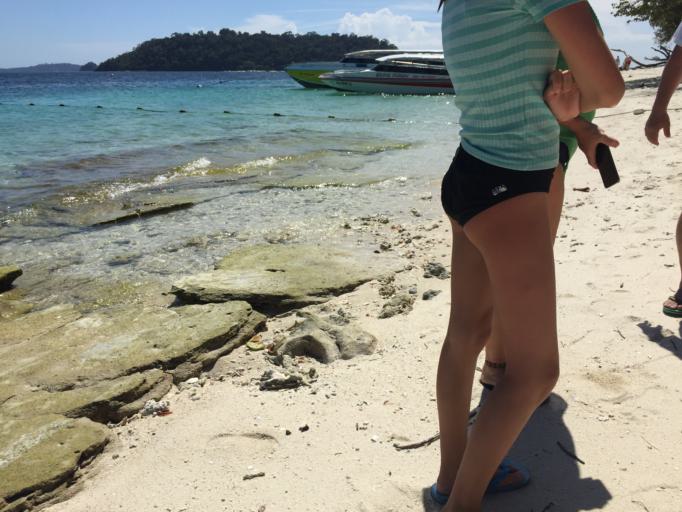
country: TH
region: Satun
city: La-ngu
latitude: 6.5574
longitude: 99.2583
